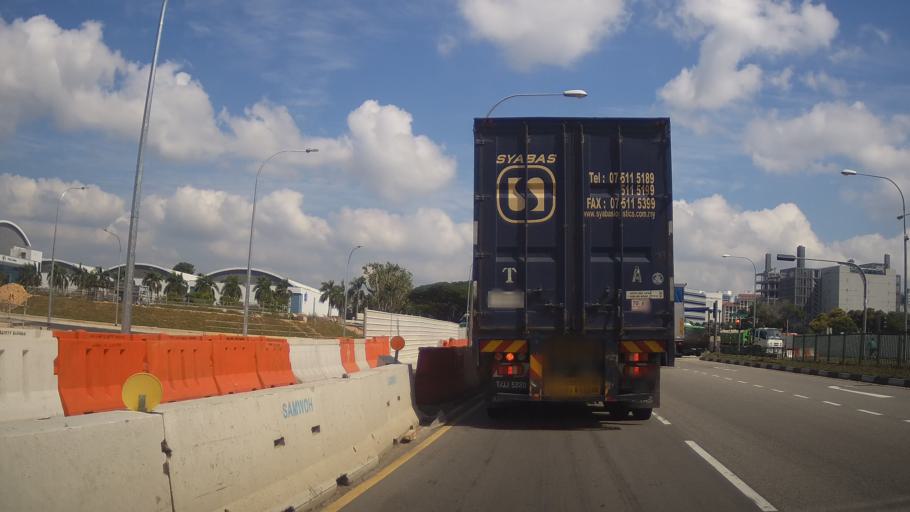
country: SG
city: Singapore
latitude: 1.3200
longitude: 103.7202
